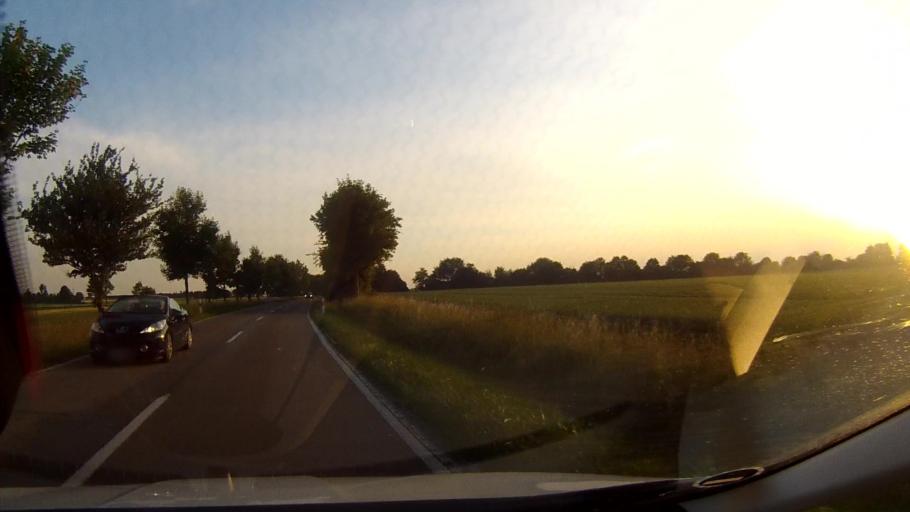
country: DE
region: Baden-Wuerttemberg
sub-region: Tuebingen Region
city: Huttisheim
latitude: 48.2854
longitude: 9.9650
